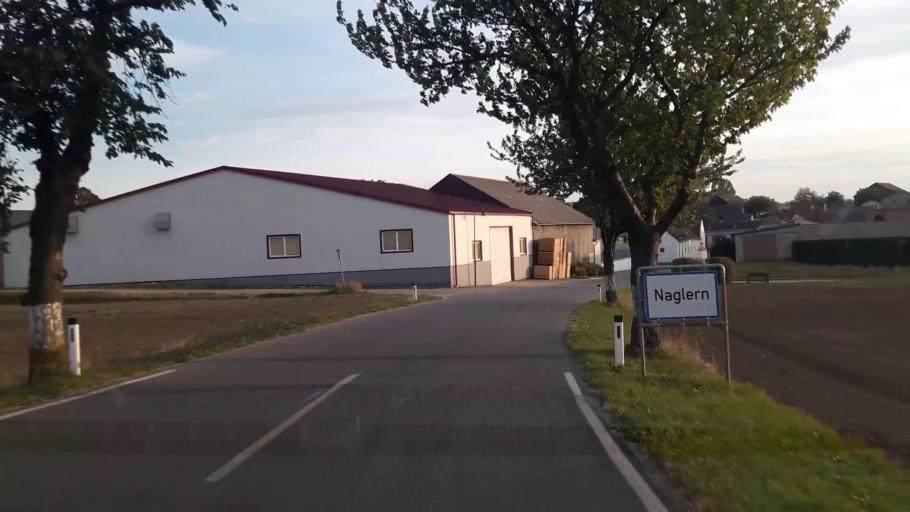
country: AT
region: Lower Austria
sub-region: Politischer Bezirk Korneuburg
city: Ernstbrunn
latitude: 48.4992
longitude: 16.3644
